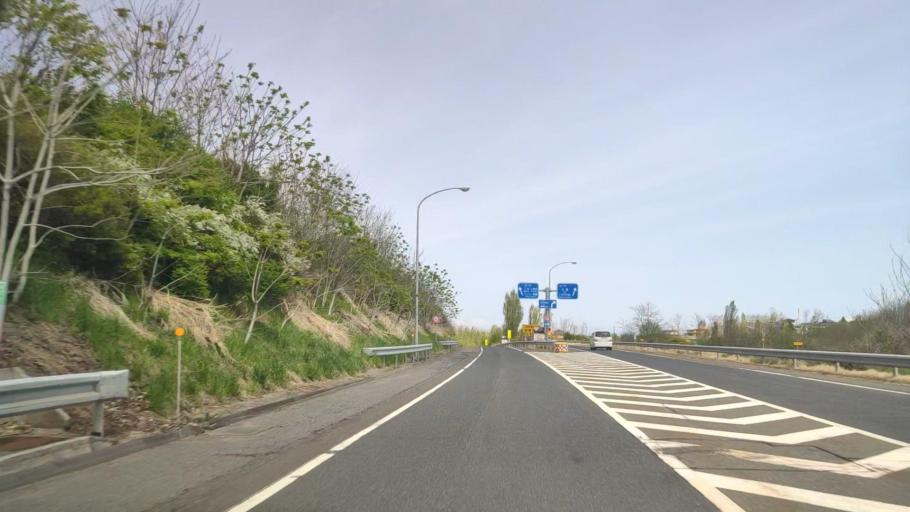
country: JP
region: Aomori
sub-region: Hachinohe Shi
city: Uchimaru
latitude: 40.4917
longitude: 141.4645
